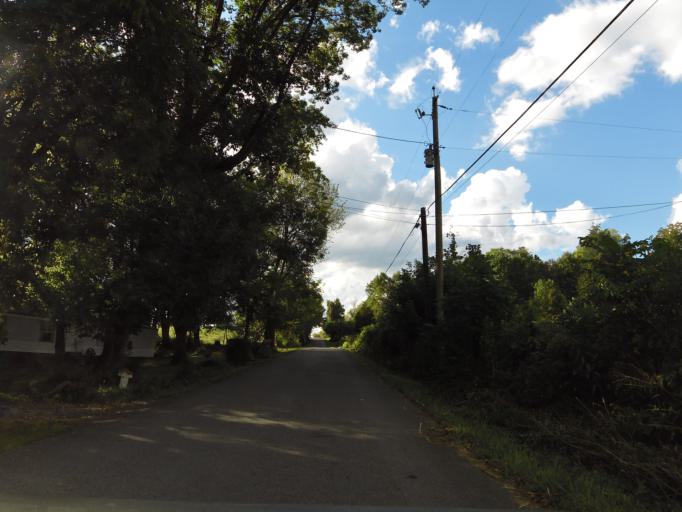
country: US
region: Tennessee
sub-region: Knox County
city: Mascot
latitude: 36.0934
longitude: -83.7819
